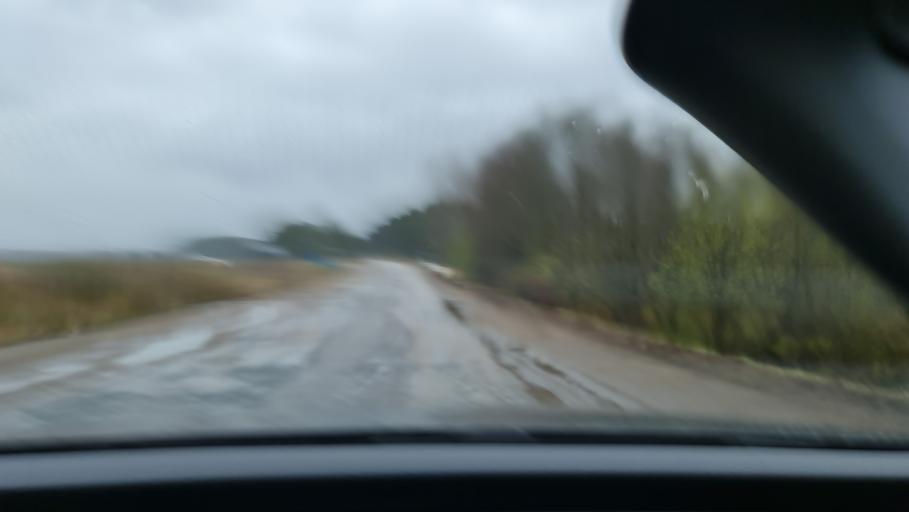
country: RU
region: Novgorod
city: Valday
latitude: 58.0392
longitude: 32.9305
